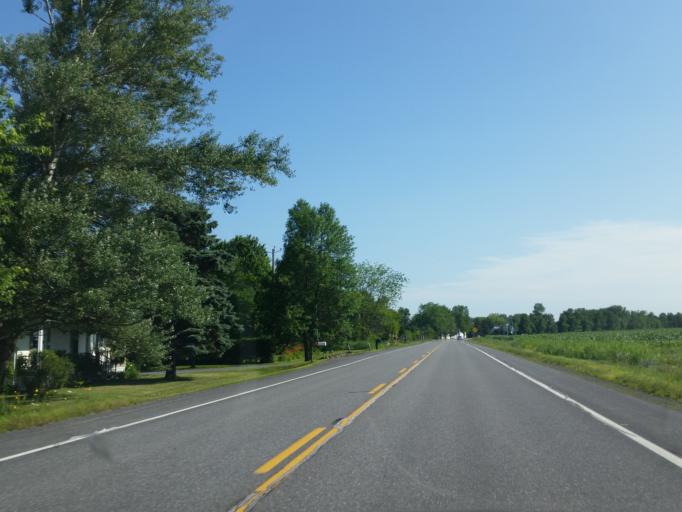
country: CA
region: Quebec
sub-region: Monteregie
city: Napierville
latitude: 45.2546
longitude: -73.3857
